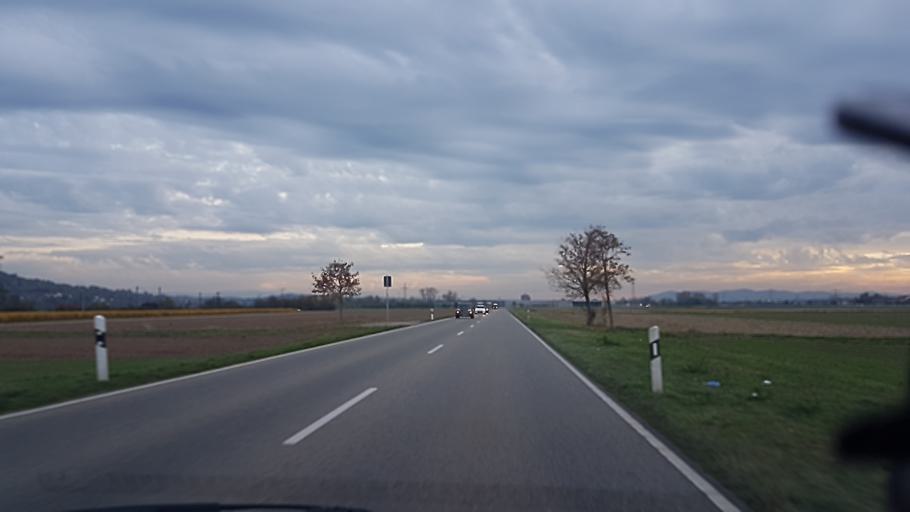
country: DE
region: Baden-Wuerttemberg
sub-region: Freiburg Region
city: Ringsheim
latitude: 48.2411
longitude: 7.7676
